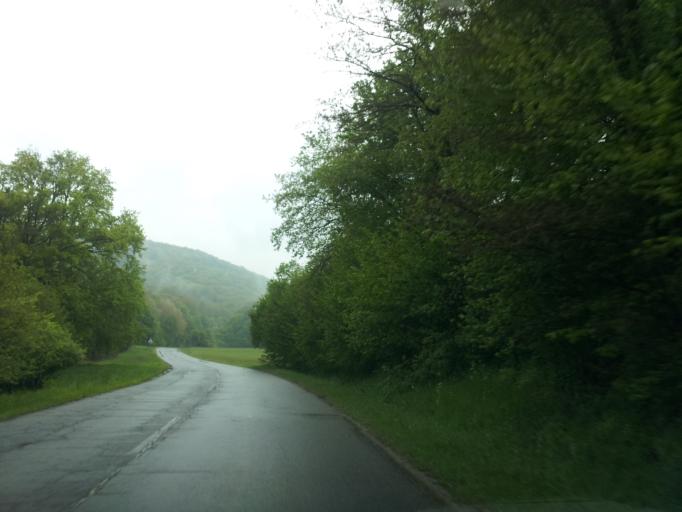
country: HU
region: Baranya
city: Komlo
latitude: 46.2004
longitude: 18.3032
